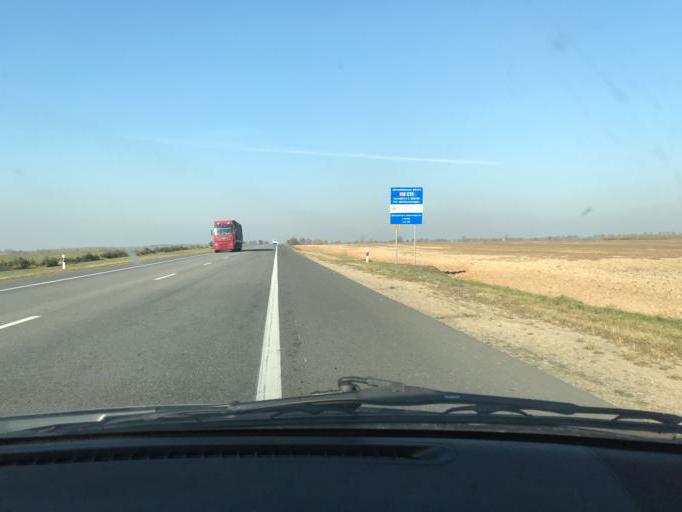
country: BY
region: Mogilev
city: Shklow
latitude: 54.3011
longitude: 30.4482
